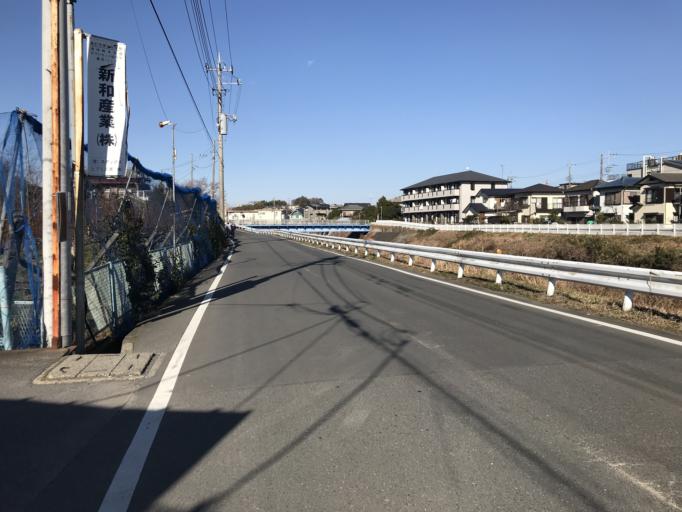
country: JP
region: Tokyo
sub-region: Machida-shi
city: Machida
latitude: 35.5743
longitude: 139.5087
